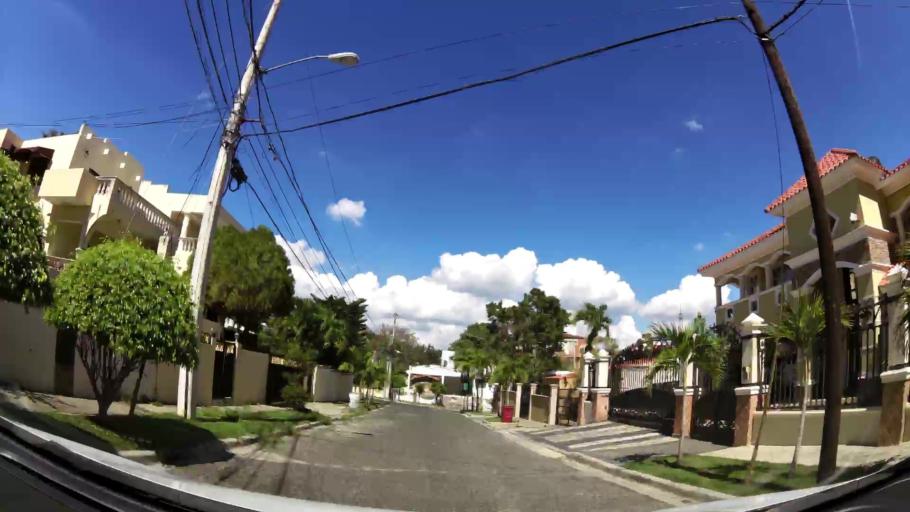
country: DO
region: Santiago
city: Santiago de los Caballeros
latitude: 19.4472
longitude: -70.6917
